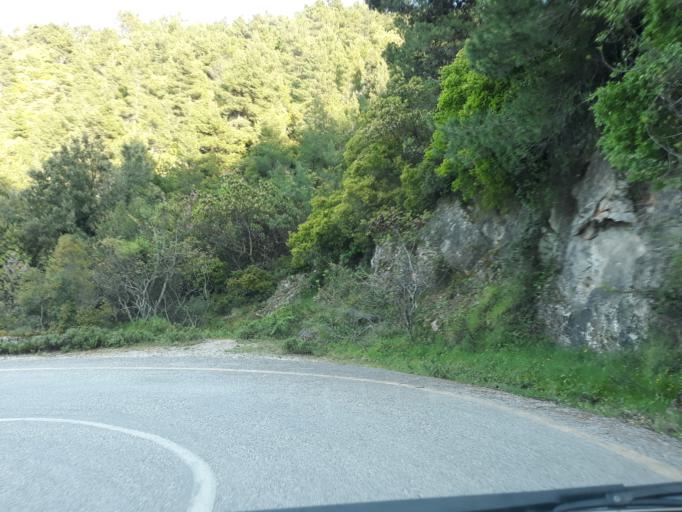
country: GR
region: Attica
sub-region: Nomarchia Anatolikis Attikis
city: Afidnes
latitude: 38.2206
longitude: 23.7828
